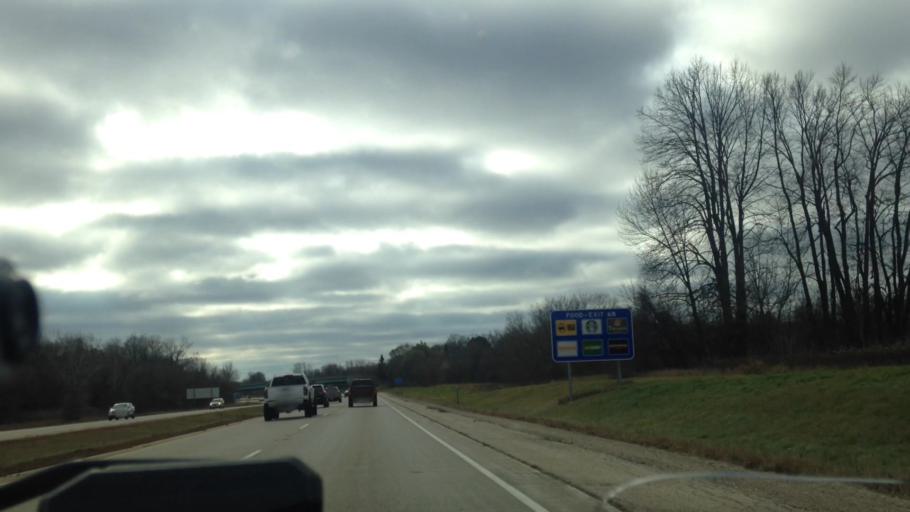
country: US
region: Wisconsin
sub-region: Washington County
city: West Bend
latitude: 43.4171
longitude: -88.2070
